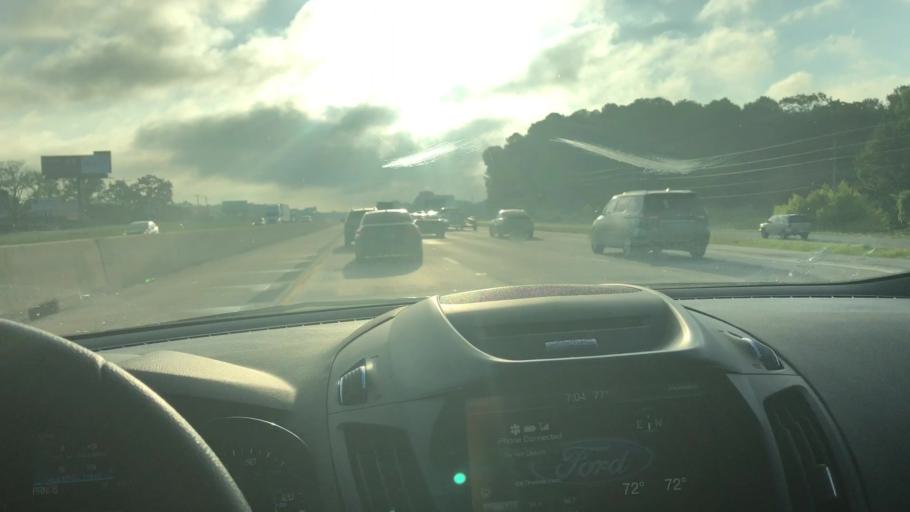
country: US
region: Arkansas
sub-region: Pulaski County
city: Alexander
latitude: 34.6344
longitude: -92.4604
